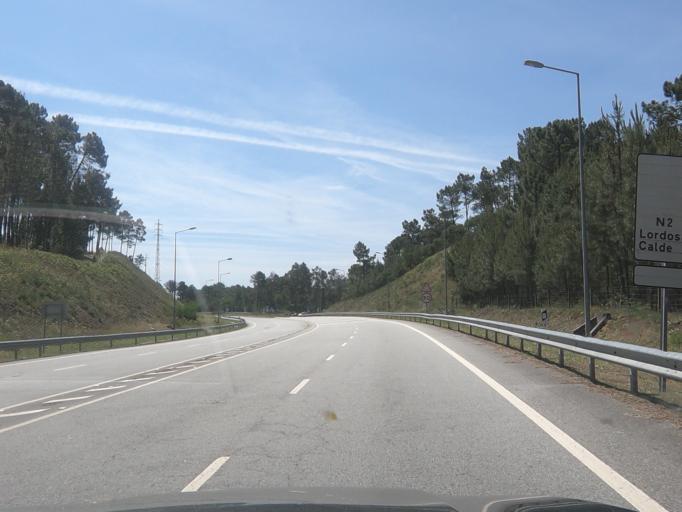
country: PT
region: Viseu
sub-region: Viseu
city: Campo
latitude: 40.7052
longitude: -7.9439
